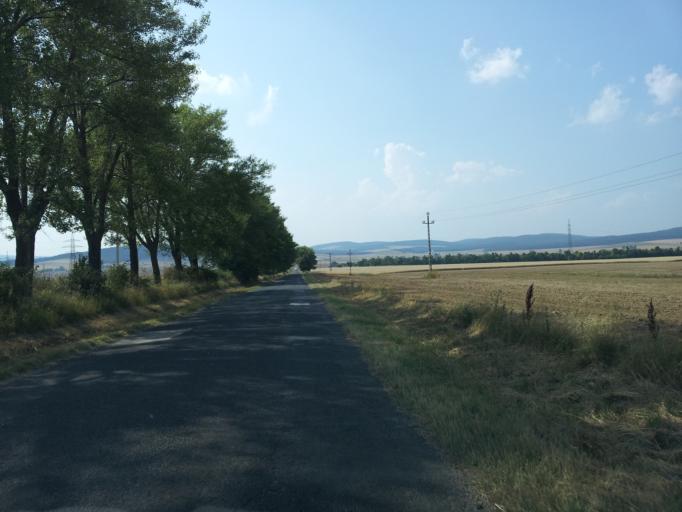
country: HU
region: Veszprem
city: Nemesvamos
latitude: 47.0192
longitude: 17.8057
